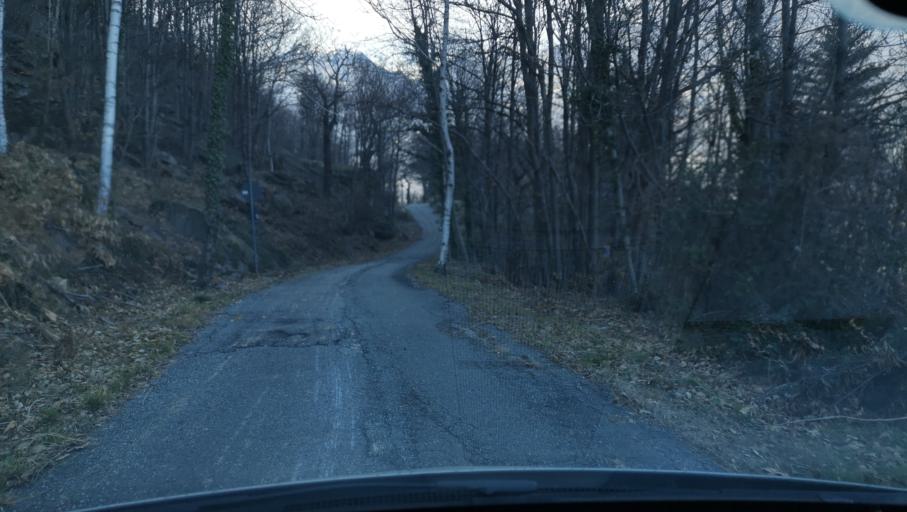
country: IT
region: Piedmont
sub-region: Provincia di Torino
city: Tavagnasco
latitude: 45.5425
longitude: 7.8166
